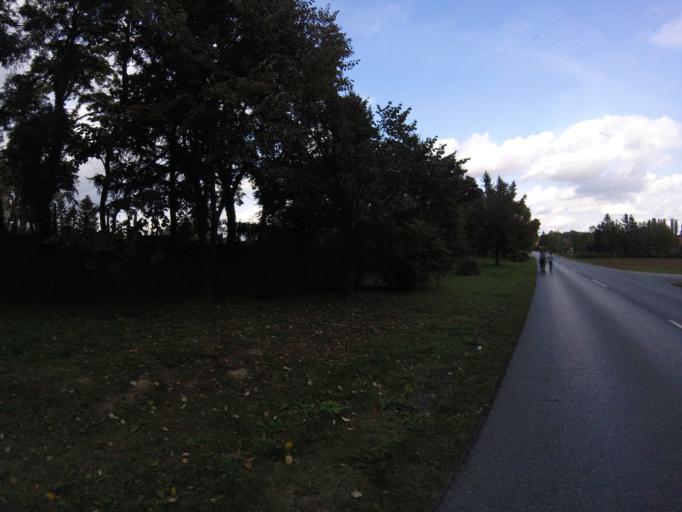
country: HU
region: Vas
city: Csepreg
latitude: 47.3946
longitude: 16.7031
